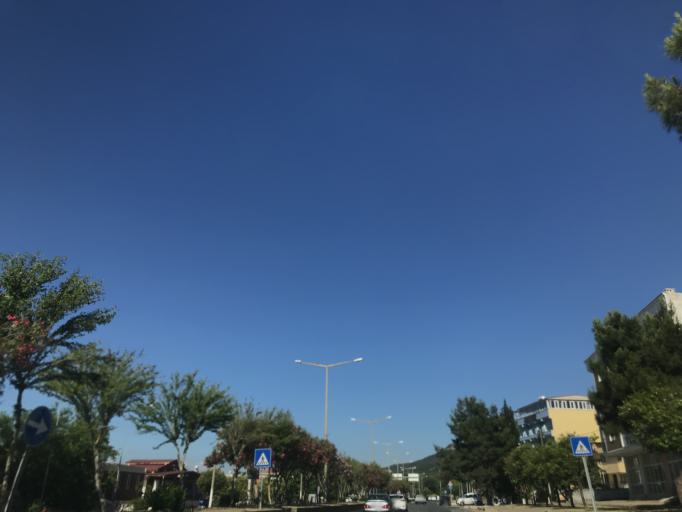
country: TR
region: Aydin
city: Davutlar
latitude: 37.7155
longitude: 27.2292
